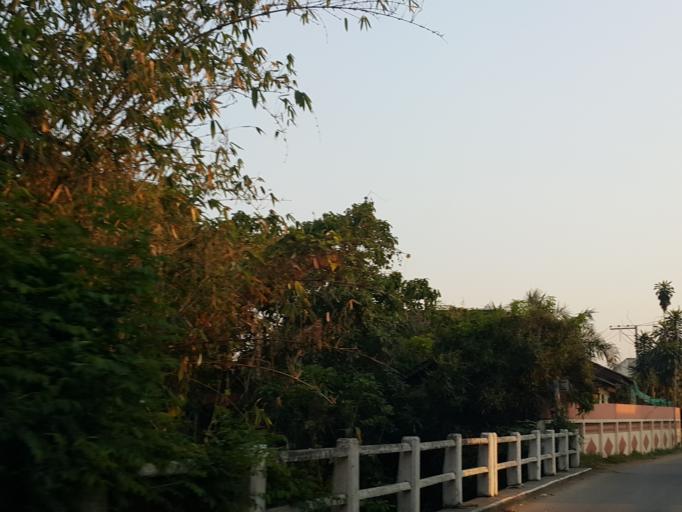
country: TH
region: Chiang Mai
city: San Sai
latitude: 18.8943
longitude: 98.9609
